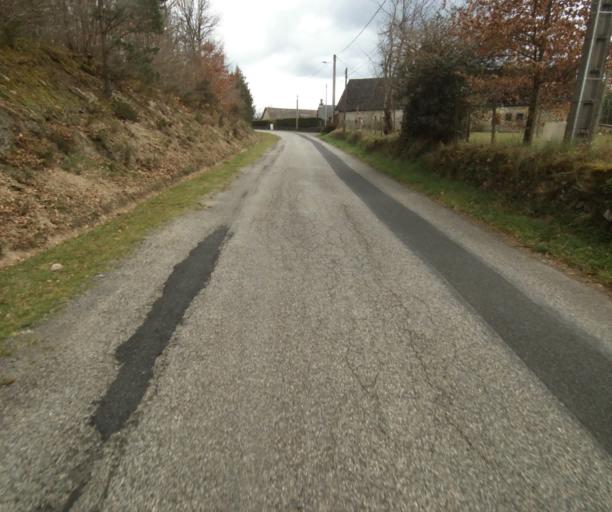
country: FR
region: Limousin
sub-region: Departement de la Correze
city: Correze
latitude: 45.2840
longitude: 1.9698
